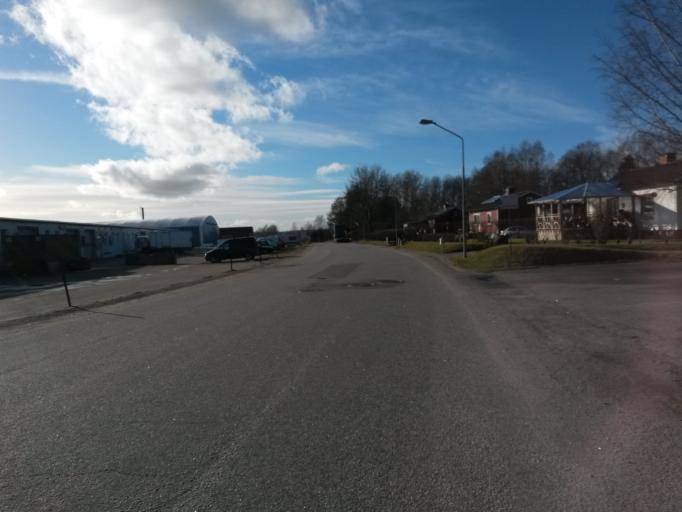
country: SE
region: Vaestra Goetaland
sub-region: Vargarda Kommun
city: Vargarda
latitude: 58.0301
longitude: 12.7959
